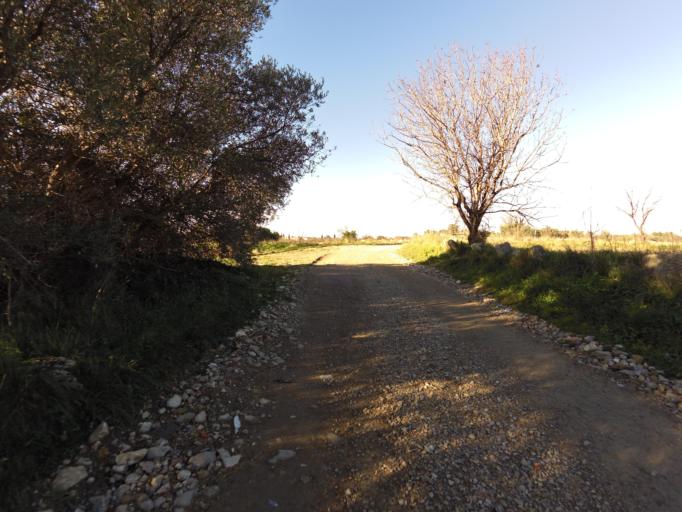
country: FR
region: Languedoc-Roussillon
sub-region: Departement du Gard
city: Aigues-Vives
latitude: 43.7449
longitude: 4.1782
